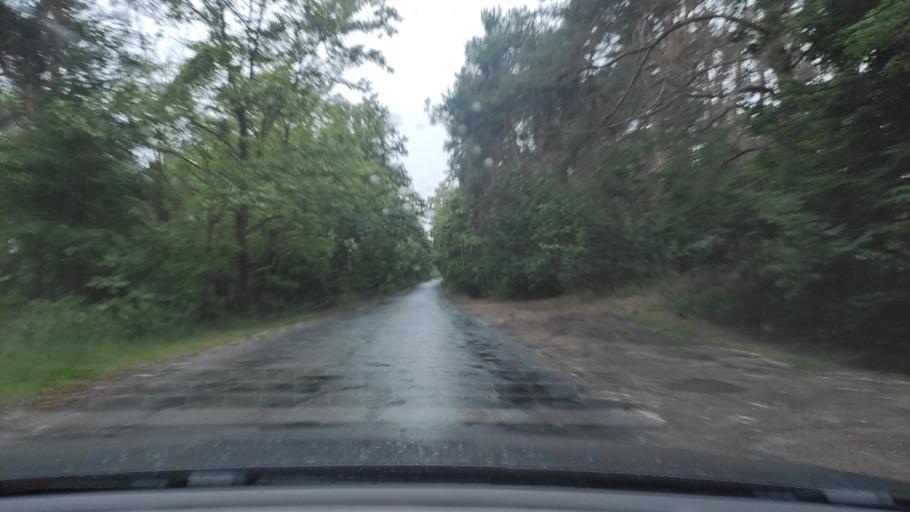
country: PL
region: Greater Poland Voivodeship
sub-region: Powiat poznanski
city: Kostrzyn
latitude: 52.4554
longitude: 17.1634
